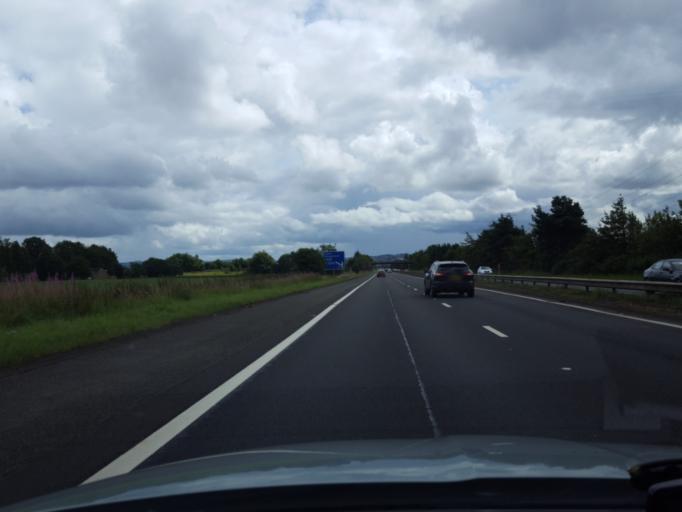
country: GB
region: Scotland
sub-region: Falkirk
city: Airth
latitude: 56.0336
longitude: -3.7666
